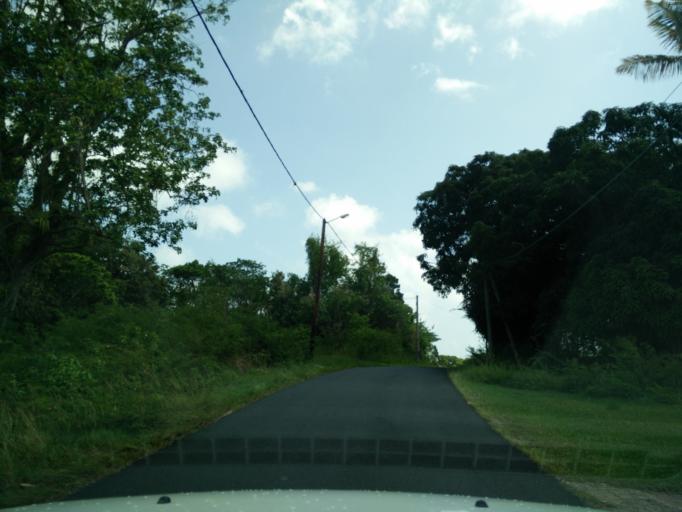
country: GP
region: Guadeloupe
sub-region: Guadeloupe
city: Grand-Bourg
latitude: 15.9088
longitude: -61.2765
